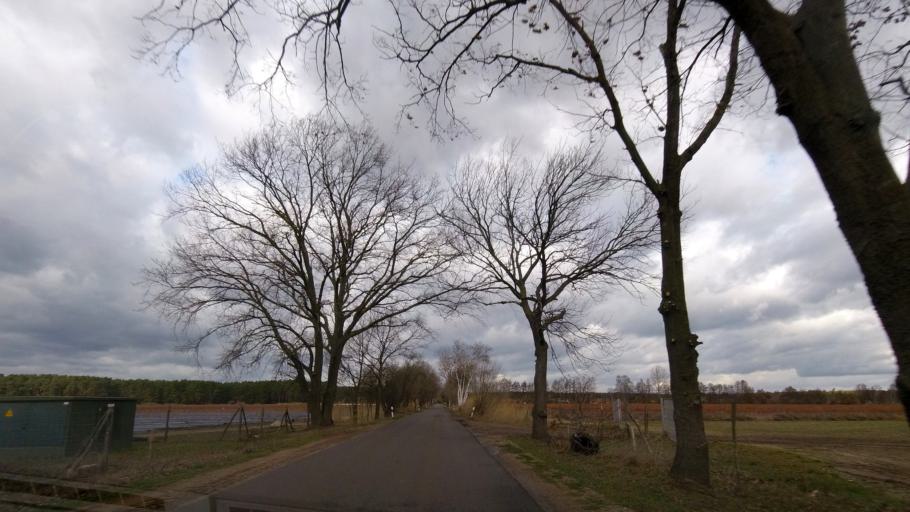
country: DE
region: Brandenburg
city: Borkheide
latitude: 52.2009
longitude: 12.9038
